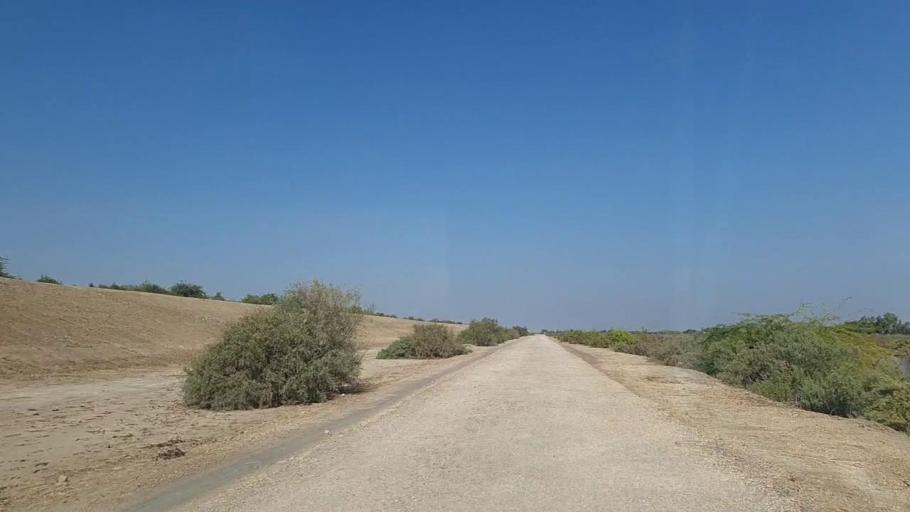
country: PK
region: Sindh
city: Chuhar Jamali
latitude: 24.4550
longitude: 67.9994
